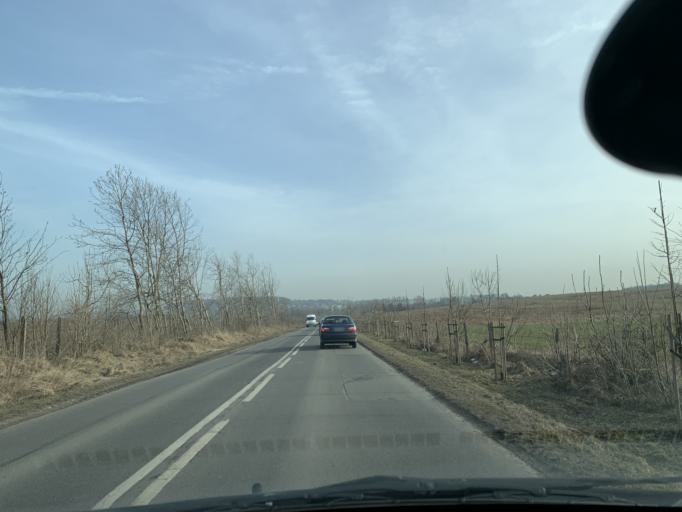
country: PL
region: Silesian Voivodeship
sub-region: Powiat tarnogorski
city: Radzionkow
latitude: 50.4141
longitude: 18.8894
